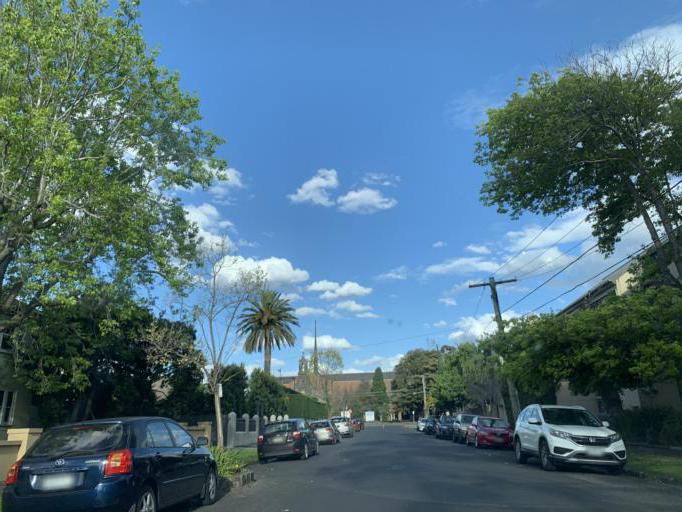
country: AU
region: Victoria
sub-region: Bayside
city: North Brighton
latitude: -37.9113
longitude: 144.9907
